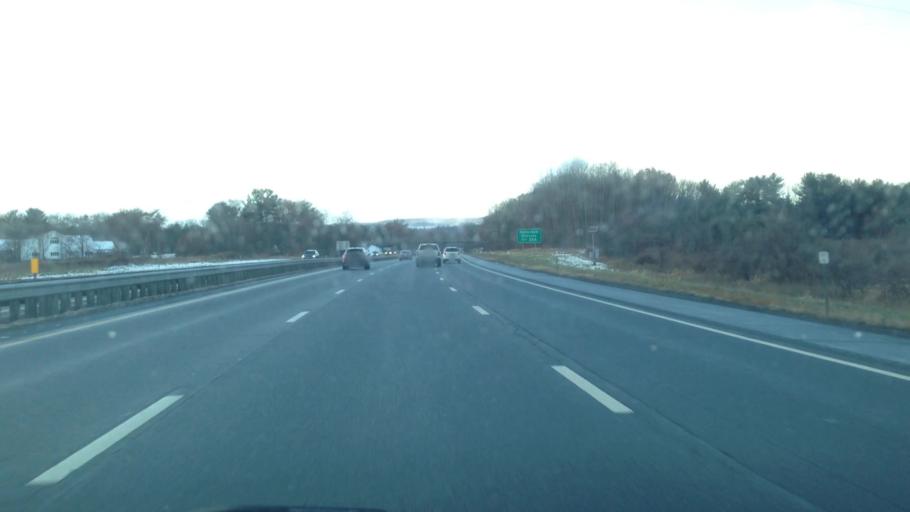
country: US
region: New York
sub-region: Schenectady County
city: Rotterdam
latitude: 42.7774
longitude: -73.9977
